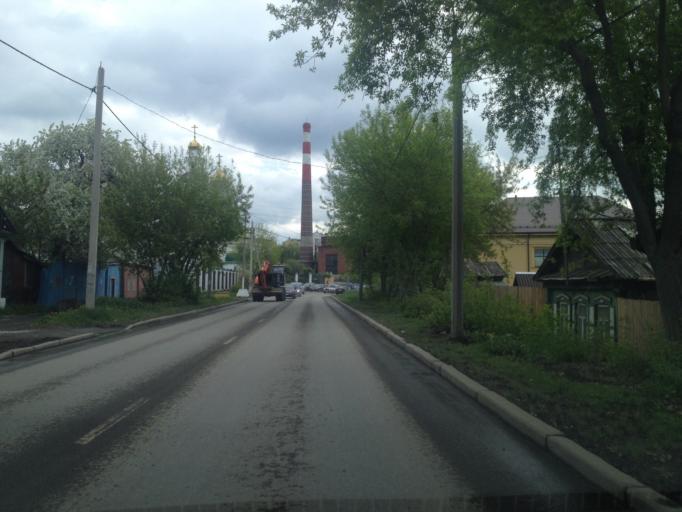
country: RU
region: Sverdlovsk
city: Yekaterinburg
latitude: 56.7798
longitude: 60.6470
